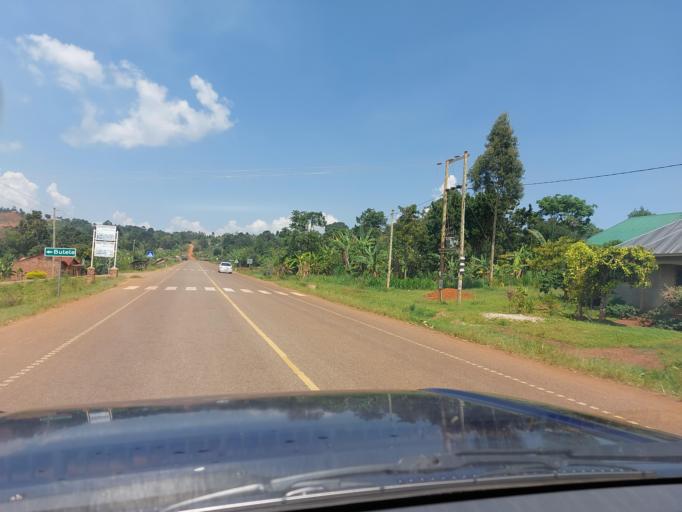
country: UG
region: Central Region
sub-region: Buikwe District
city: Buikwe
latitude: 0.2886
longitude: 33.0868
